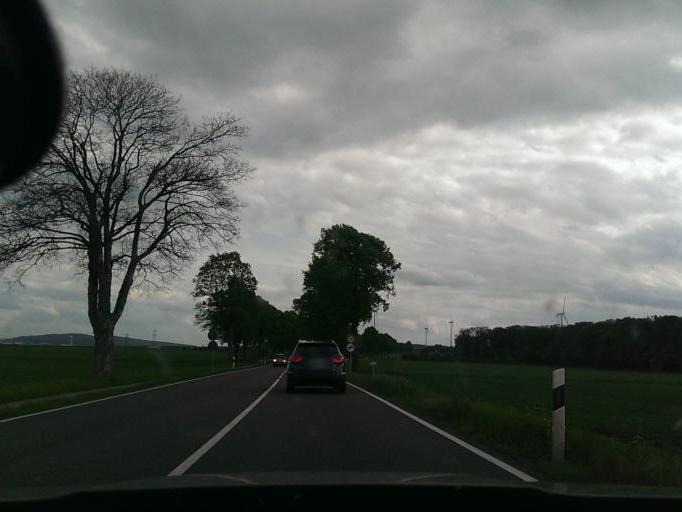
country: DE
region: Lower Saxony
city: Pattensen
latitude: 52.2089
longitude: 9.7459
